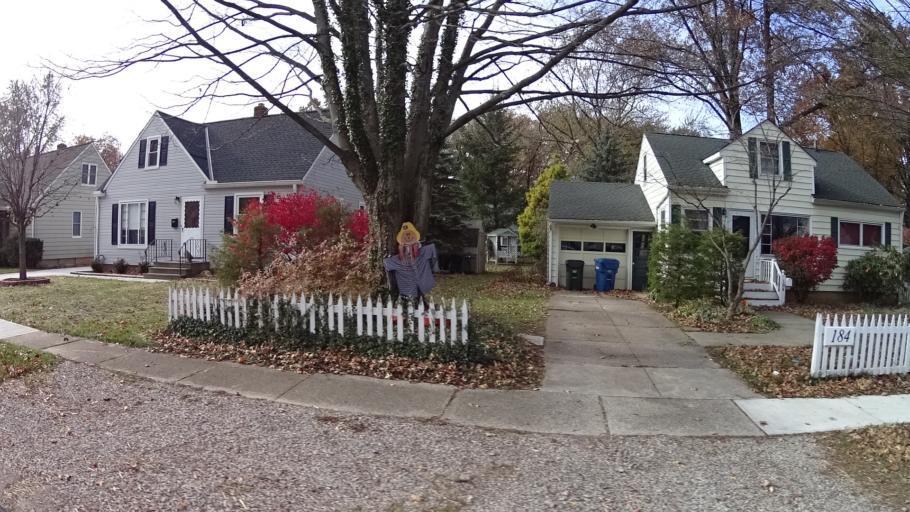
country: US
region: Ohio
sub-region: Lorain County
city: Avon Lake
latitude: 41.5074
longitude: -82.0236
